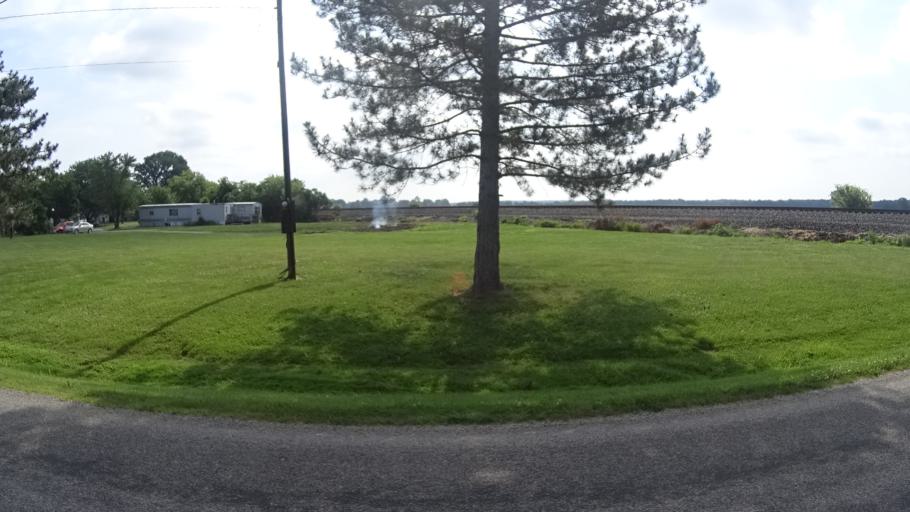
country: US
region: Ohio
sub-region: Lorain County
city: Vermilion
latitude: 41.3890
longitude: -82.4304
